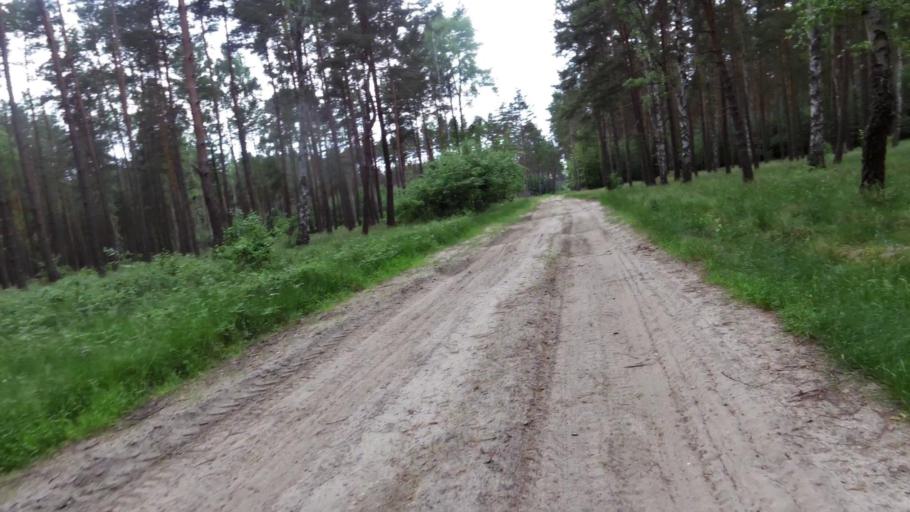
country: PL
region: West Pomeranian Voivodeship
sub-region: Powiat mysliborski
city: Debno
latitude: 52.8340
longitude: 14.6278
